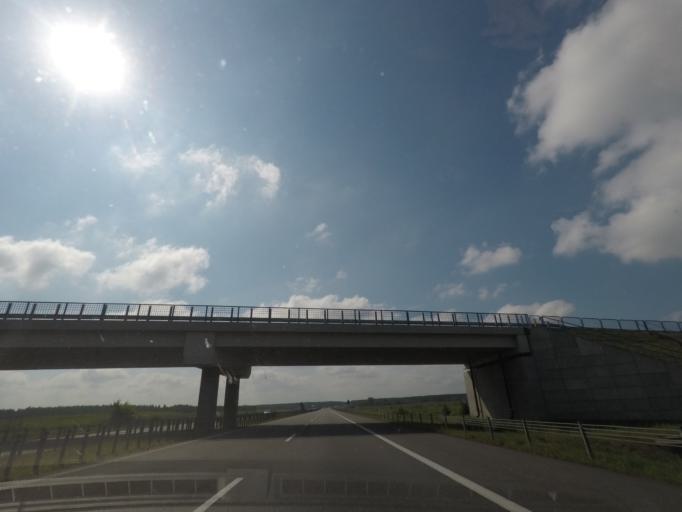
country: PL
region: Kujawsko-Pomorskie
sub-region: Powiat wabrzeski
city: Pluznica
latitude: 53.1716
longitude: 18.7403
